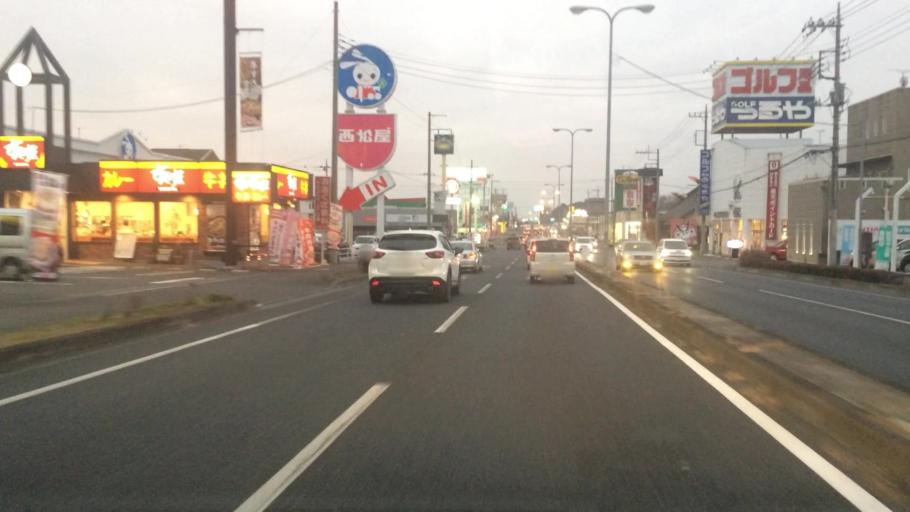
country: JP
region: Tochigi
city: Utsunomiya-shi
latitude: 36.5602
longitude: 139.8509
